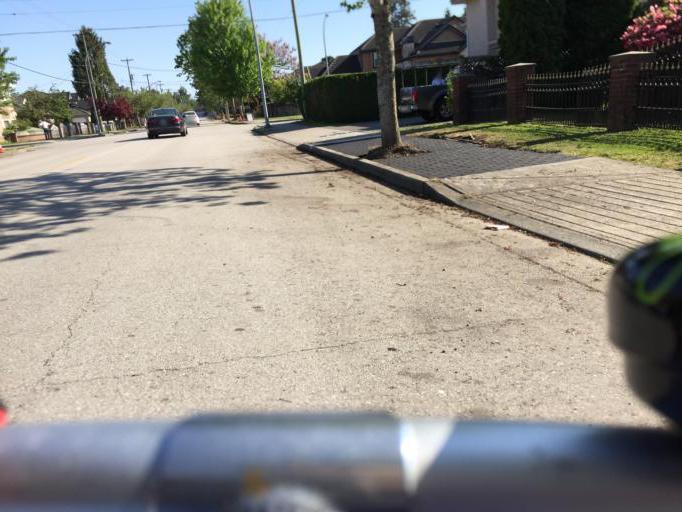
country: CA
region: British Columbia
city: Richmond
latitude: 49.1518
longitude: -123.1310
